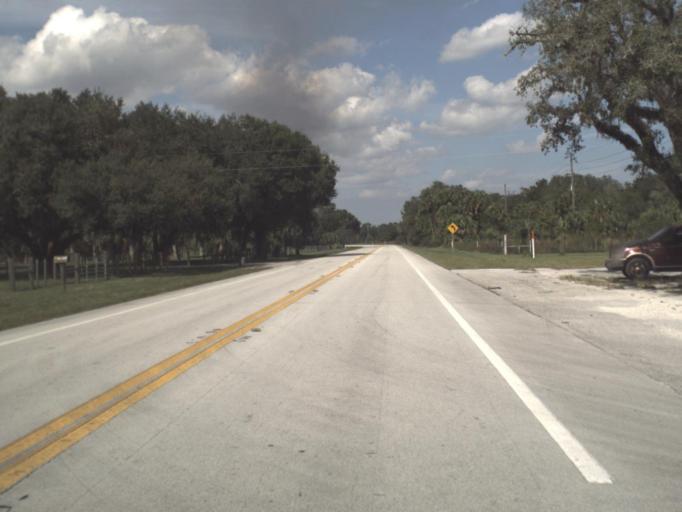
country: US
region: Florida
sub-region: Okeechobee County
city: Cypress Quarters
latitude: 27.5268
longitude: -80.8070
